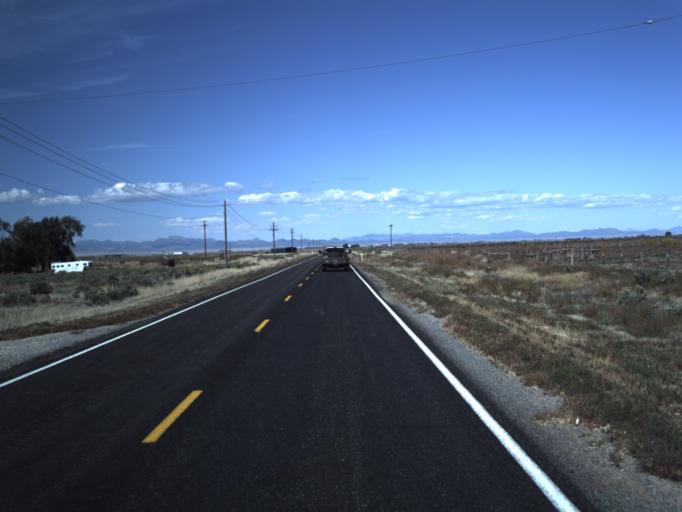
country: US
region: Utah
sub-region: Washington County
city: Enterprise
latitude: 37.6163
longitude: -113.6612
